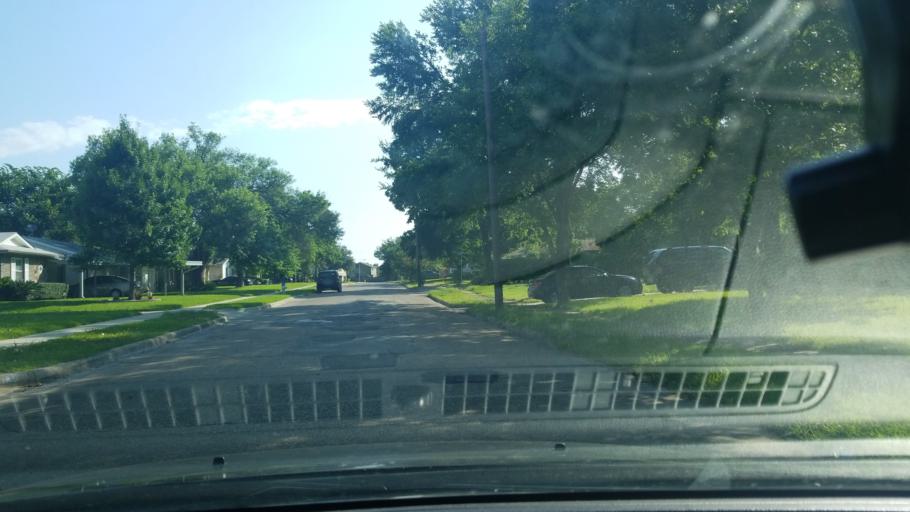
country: US
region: Texas
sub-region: Dallas County
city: Mesquite
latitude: 32.8251
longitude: -96.6358
